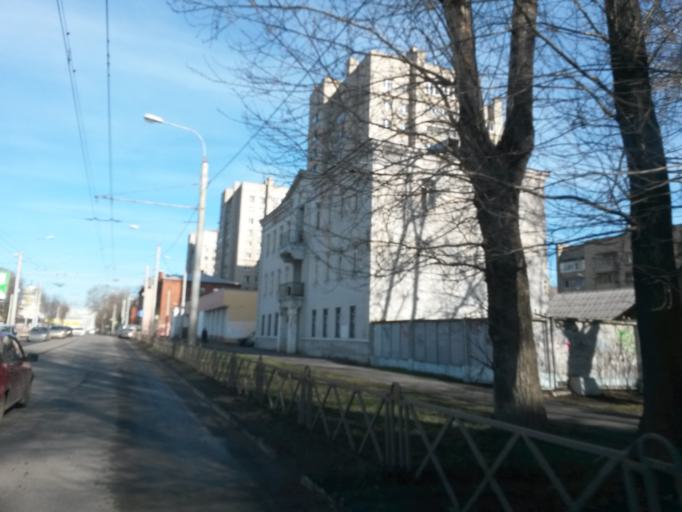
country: RU
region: Jaroslavl
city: Yaroslavl
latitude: 57.6238
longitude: 39.8414
